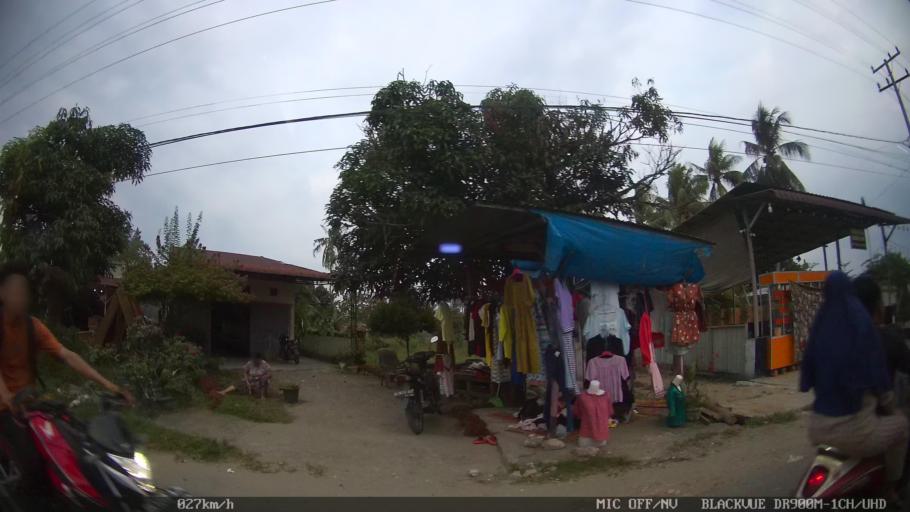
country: ID
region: North Sumatra
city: Sunggal
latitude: 3.5613
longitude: 98.5748
